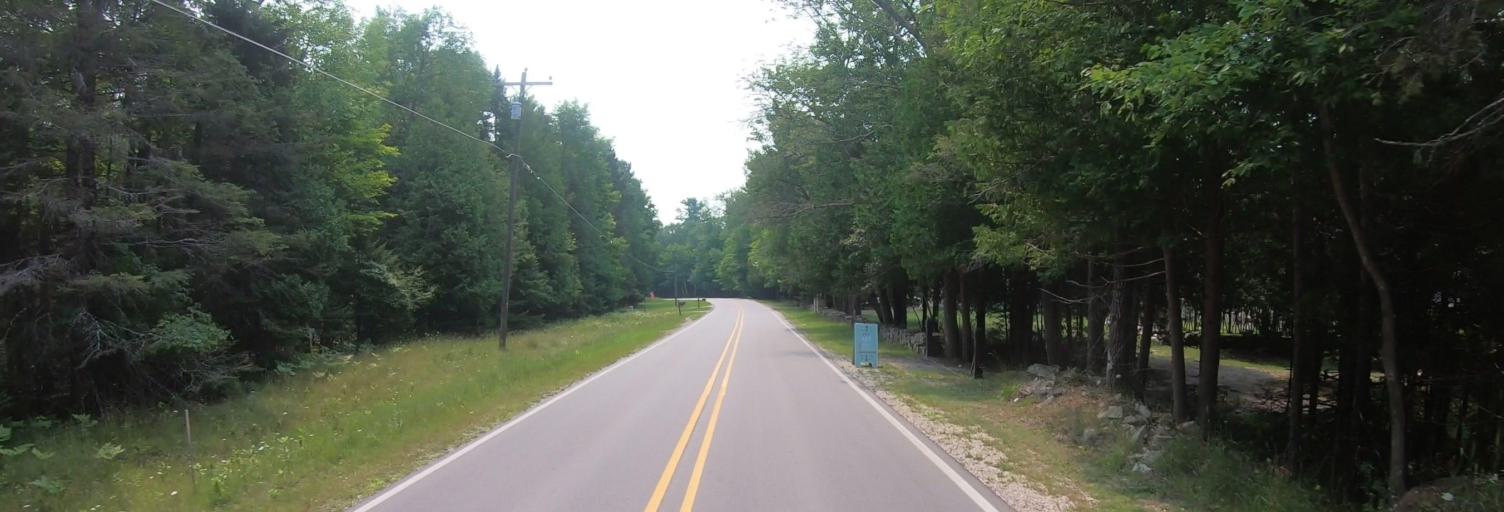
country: CA
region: Ontario
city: Thessalon
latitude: 46.0271
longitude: -83.7316
